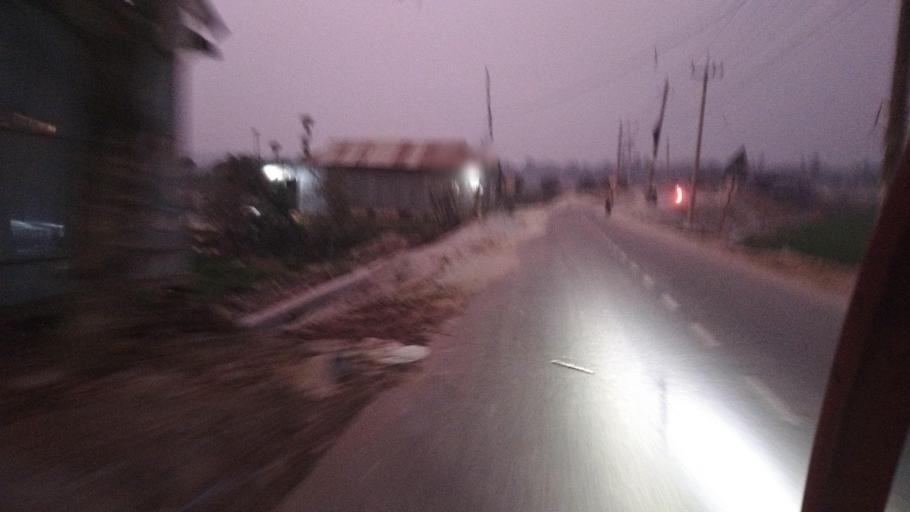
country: BD
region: Dhaka
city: Sakhipur
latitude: 24.3920
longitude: 90.3318
